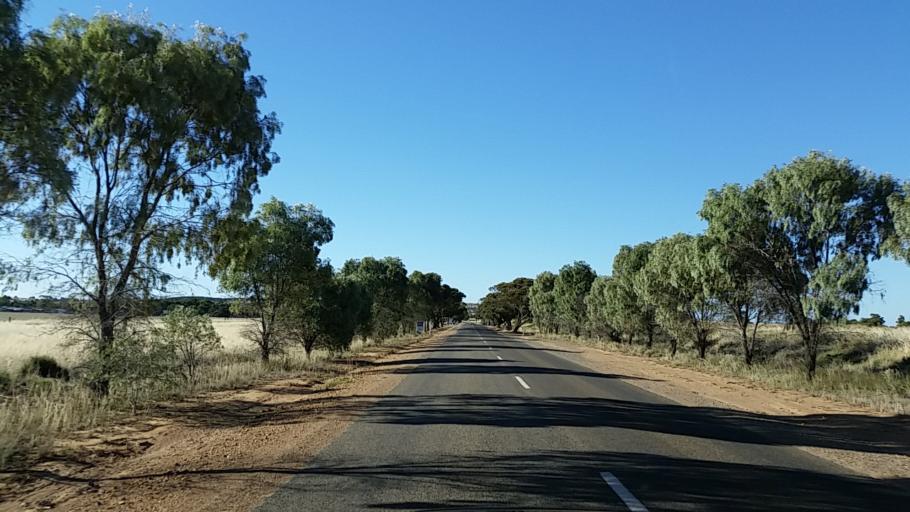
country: AU
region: South Australia
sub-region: Peterborough
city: Peterborough
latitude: -32.9829
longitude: 138.8467
